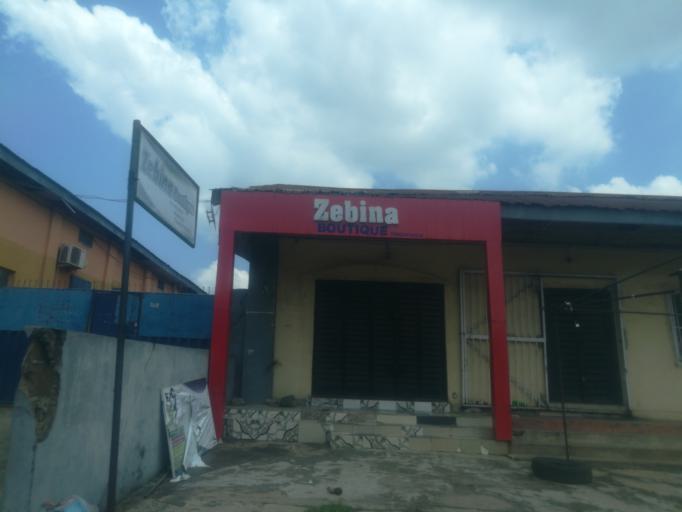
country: NG
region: Oyo
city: Ibadan
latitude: 7.3860
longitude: 3.8815
